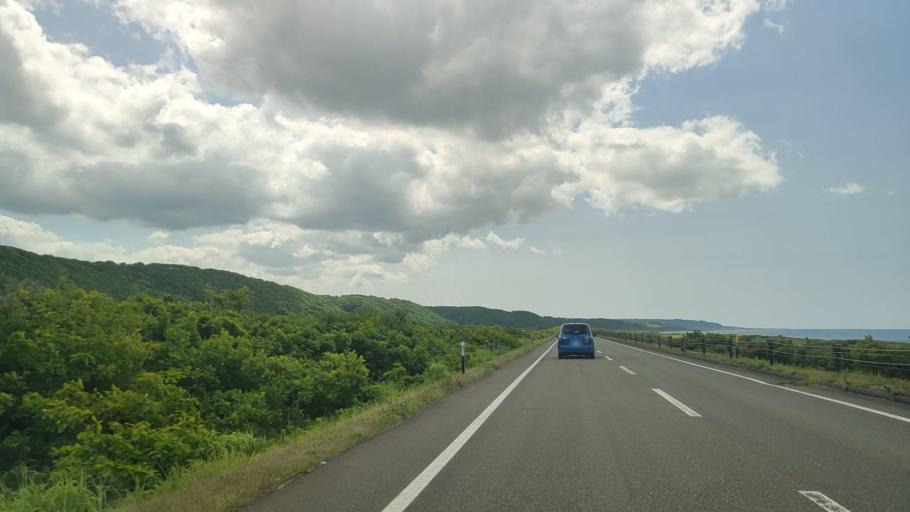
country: JP
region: Hokkaido
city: Wakkanai
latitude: 45.2942
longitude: 141.6228
